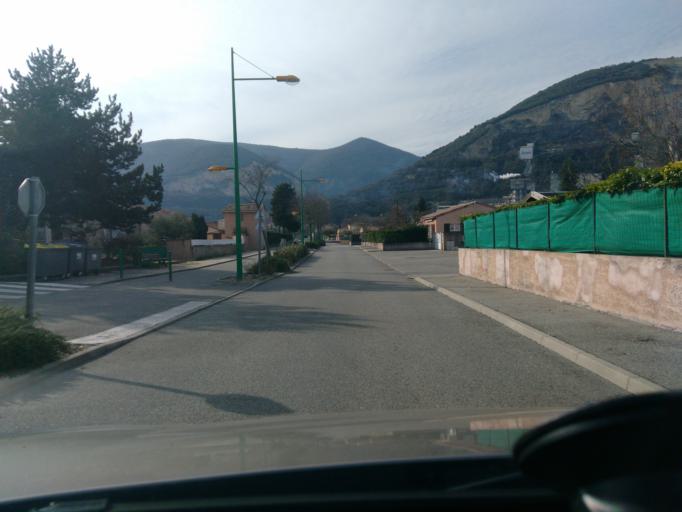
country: FR
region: Rhone-Alpes
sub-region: Departement de l'Ardeche
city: Cruas
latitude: 44.6593
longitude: 4.7711
